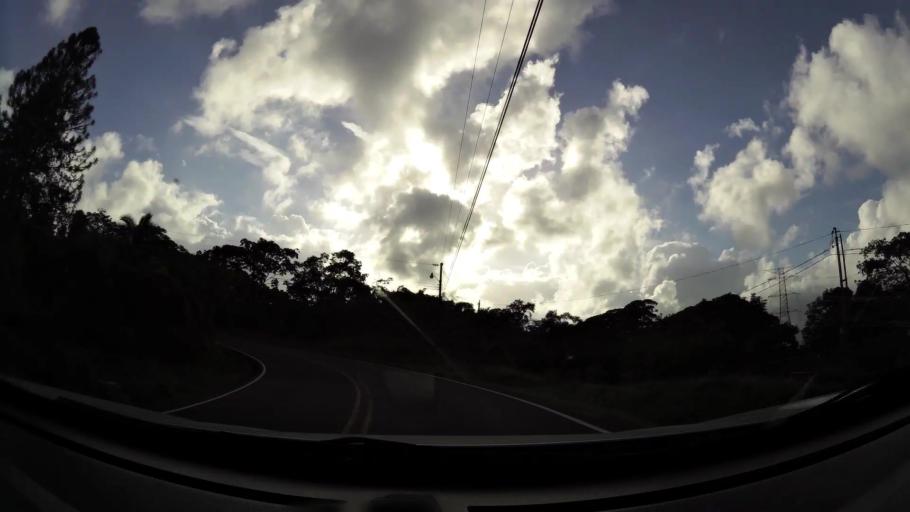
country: CR
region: Limon
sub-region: Canton de Siquirres
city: Siquirres
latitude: 10.0693
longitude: -83.5534
